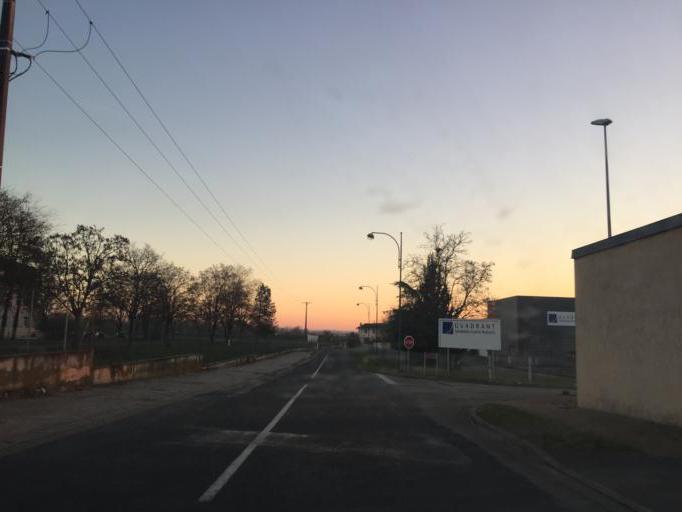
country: FR
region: Rhone-Alpes
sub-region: Departement de l'Ain
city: Balan
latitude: 45.8446
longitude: 5.1140
